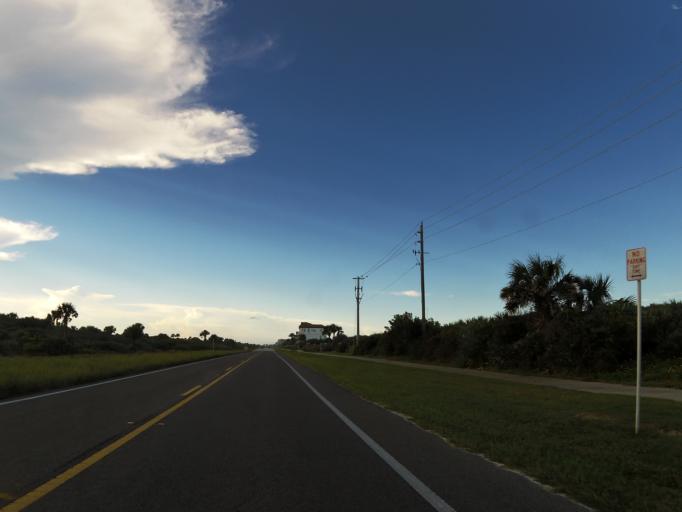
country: US
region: Florida
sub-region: Flagler County
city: Palm Coast
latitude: 29.5515
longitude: -81.1627
